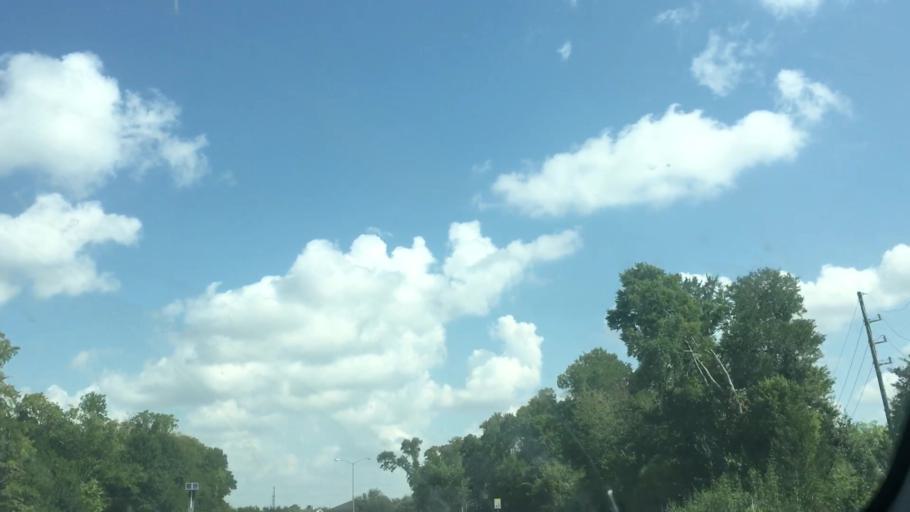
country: US
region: Texas
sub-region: Fort Bend County
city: Fifth Street
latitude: 29.5979
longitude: -95.5616
